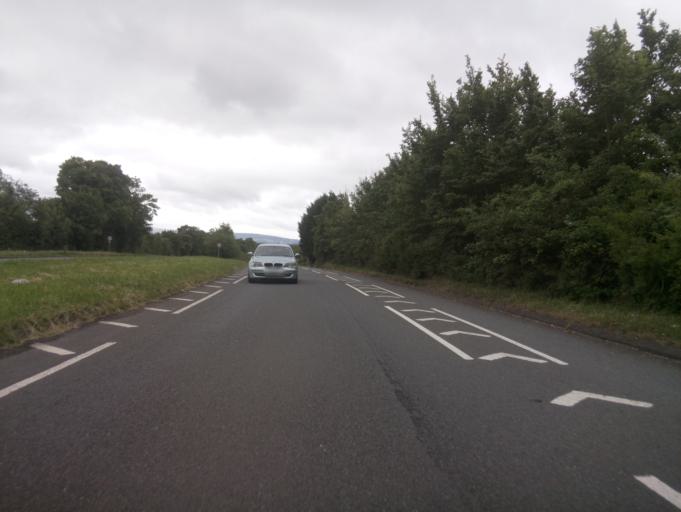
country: GB
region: England
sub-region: Gloucestershire
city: Tewkesbury
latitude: 51.9623
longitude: -2.1580
